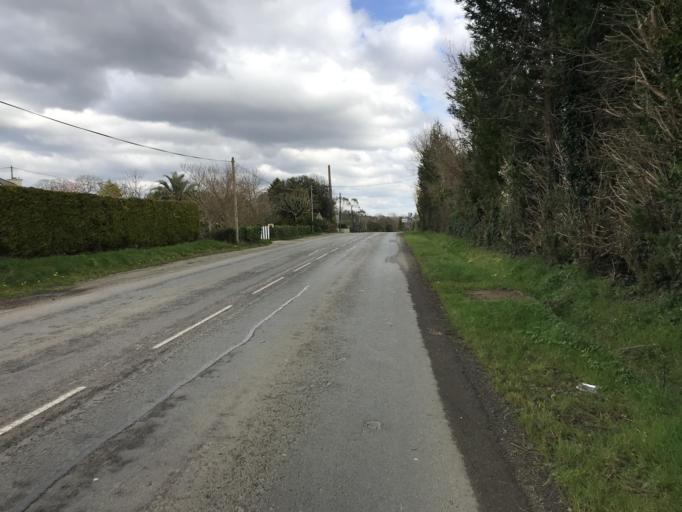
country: FR
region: Brittany
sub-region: Departement du Finistere
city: Hopital-Camfrout
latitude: 48.3255
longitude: -4.2308
